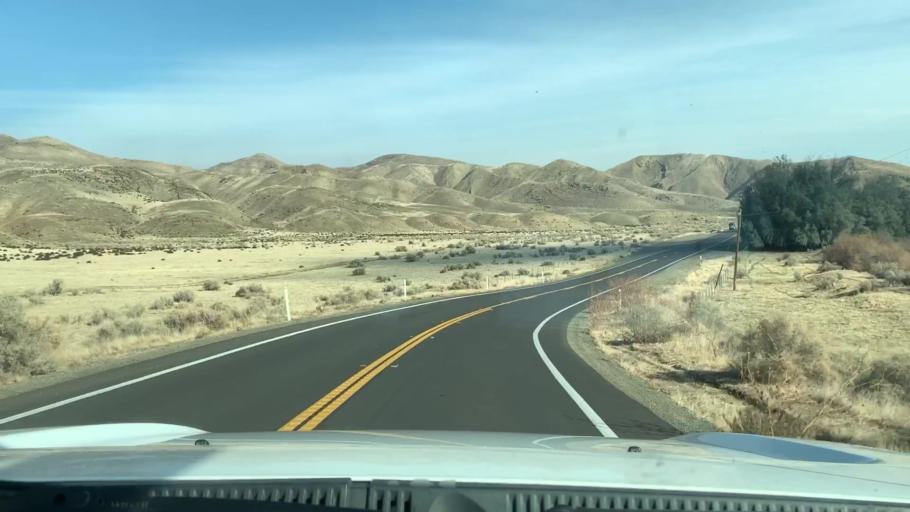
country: US
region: California
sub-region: Fresno County
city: Coalinga
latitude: 36.1042
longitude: -120.4050
